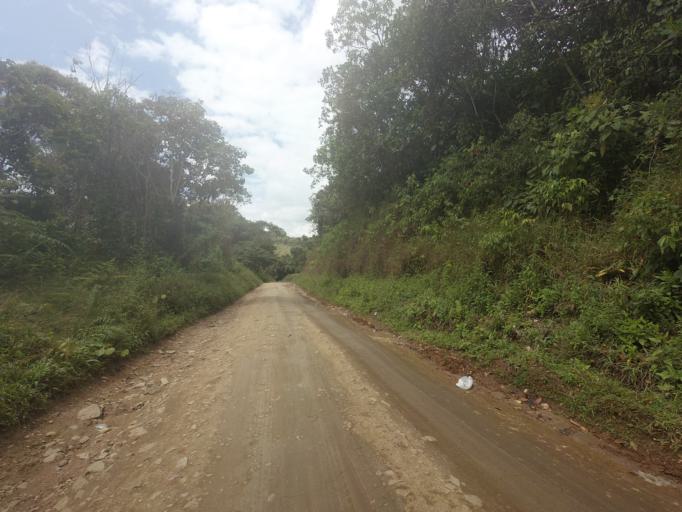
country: CO
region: Huila
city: San Agustin
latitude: 1.8881
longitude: -76.2955
